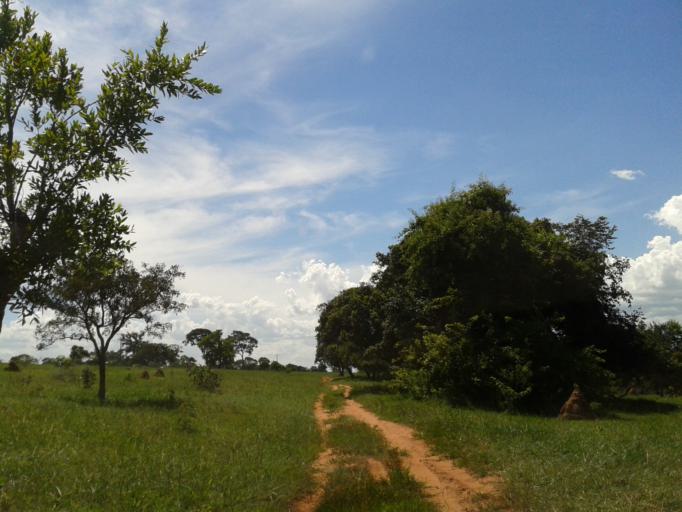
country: BR
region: Minas Gerais
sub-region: Santa Vitoria
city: Santa Vitoria
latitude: -19.1481
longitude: -50.5339
